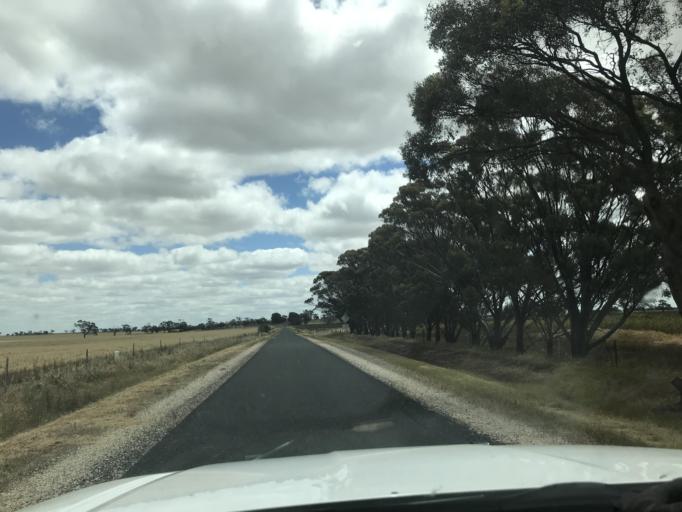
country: AU
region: South Australia
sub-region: Tatiara
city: Bordertown
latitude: -36.3571
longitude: 141.1928
